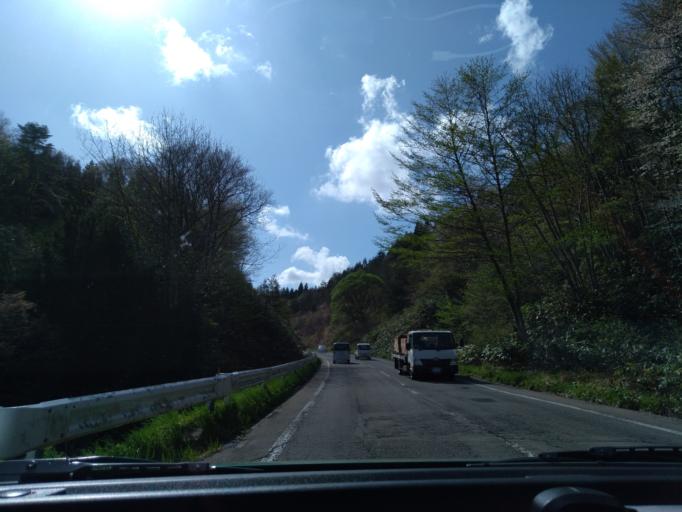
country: JP
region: Akita
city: Akita
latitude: 39.6967
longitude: 140.2565
